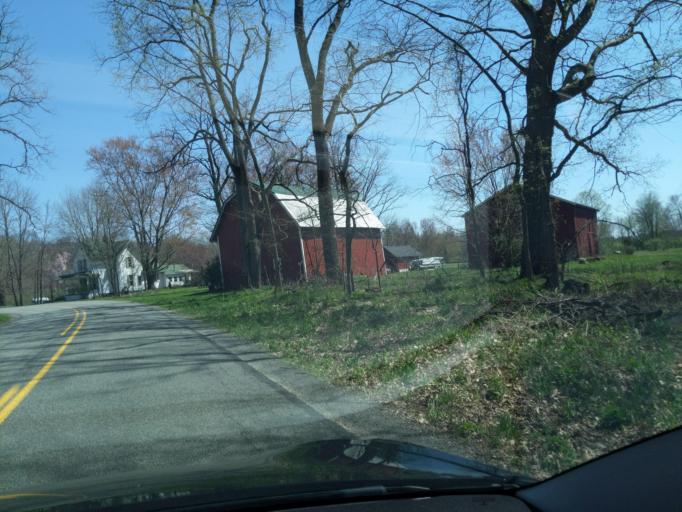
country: US
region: Michigan
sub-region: Ingham County
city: Stockbridge
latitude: 42.4834
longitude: -84.1678
